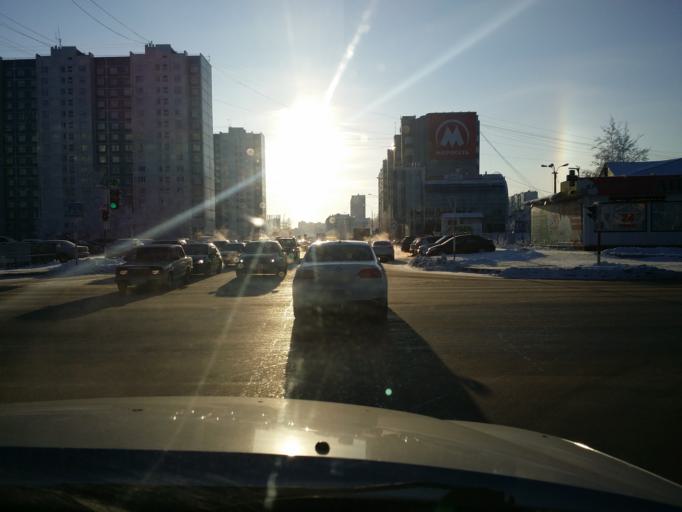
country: RU
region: Khanty-Mansiyskiy Avtonomnyy Okrug
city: Nizhnevartovsk
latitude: 60.9403
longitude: 76.5899
